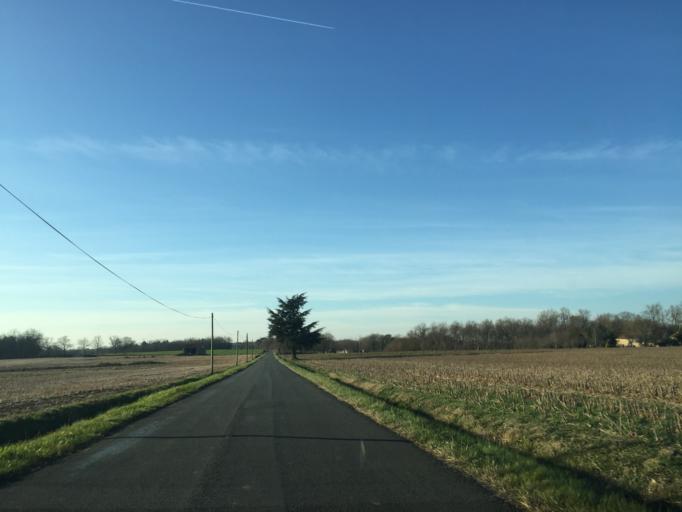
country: FR
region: Aquitaine
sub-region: Departement de la Dordogne
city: Riberac
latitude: 45.2006
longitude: 0.3296
